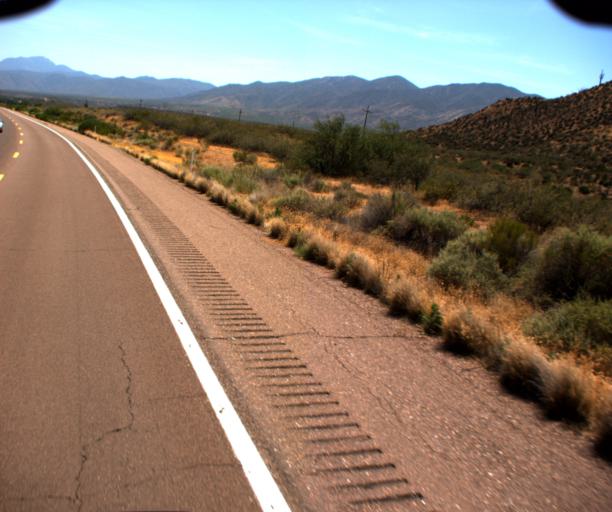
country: US
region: Arizona
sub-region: Gila County
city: Tonto Basin
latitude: 33.8885
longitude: -111.3119
